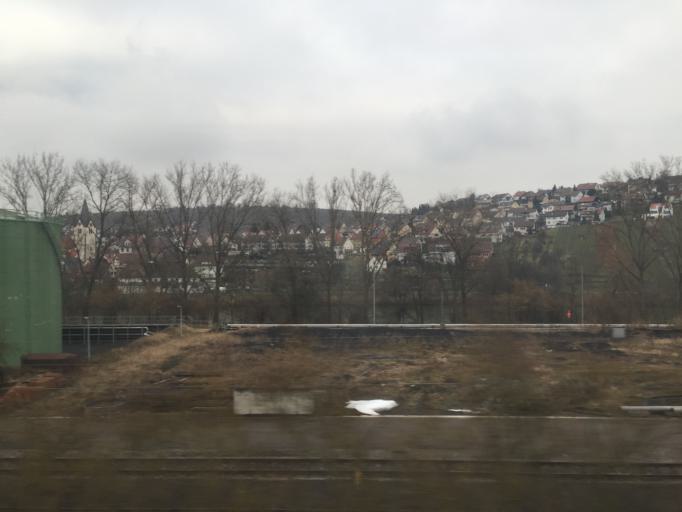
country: DE
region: Baden-Wuerttemberg
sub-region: Regierungsbezirk Stuttgart
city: Gemmrigheim
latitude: 49.0210
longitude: 9.1544
